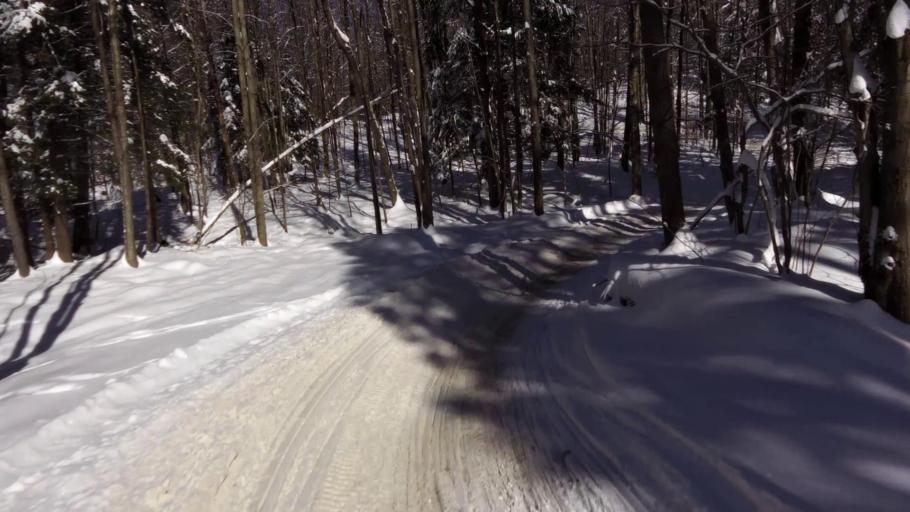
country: US
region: New York
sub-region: Chautauqua County
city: Mayville
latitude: 42.2395
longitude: -79.4230
